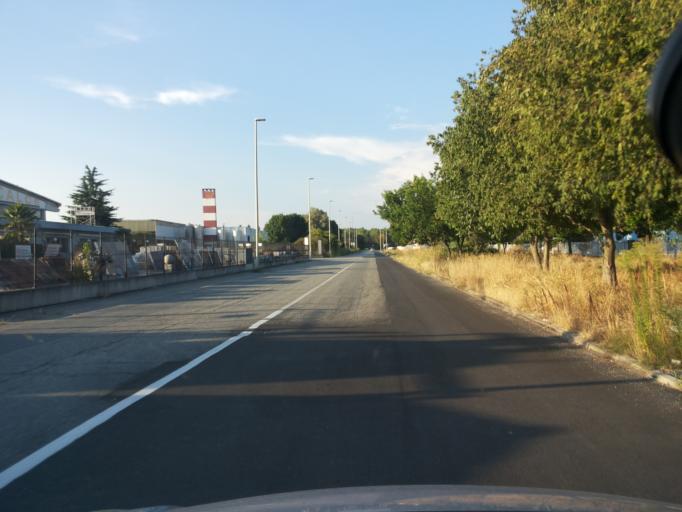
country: IT
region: Piedmont
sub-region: Provincia di Vercelli
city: Vercelli
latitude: 45.3020
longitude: 8.4072
